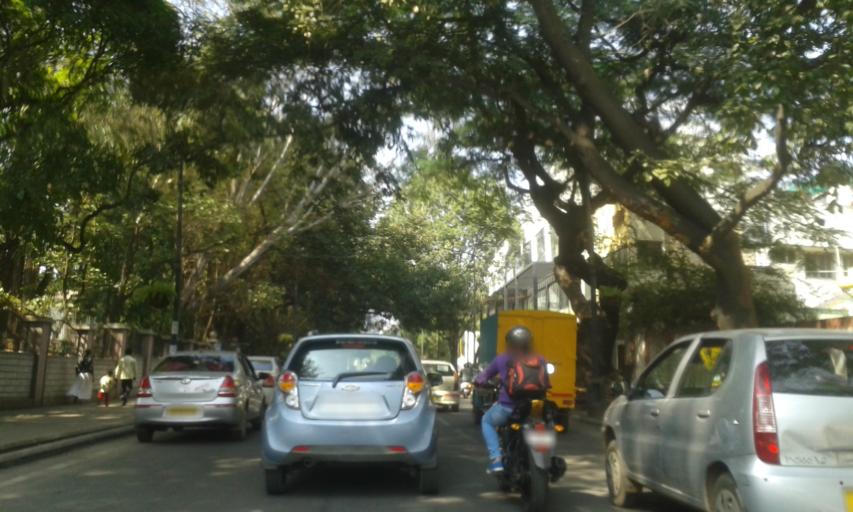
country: IN
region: Karnataka
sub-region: Bangalore Urban
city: Bangalore
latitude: 12.9729
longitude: 77.6031
